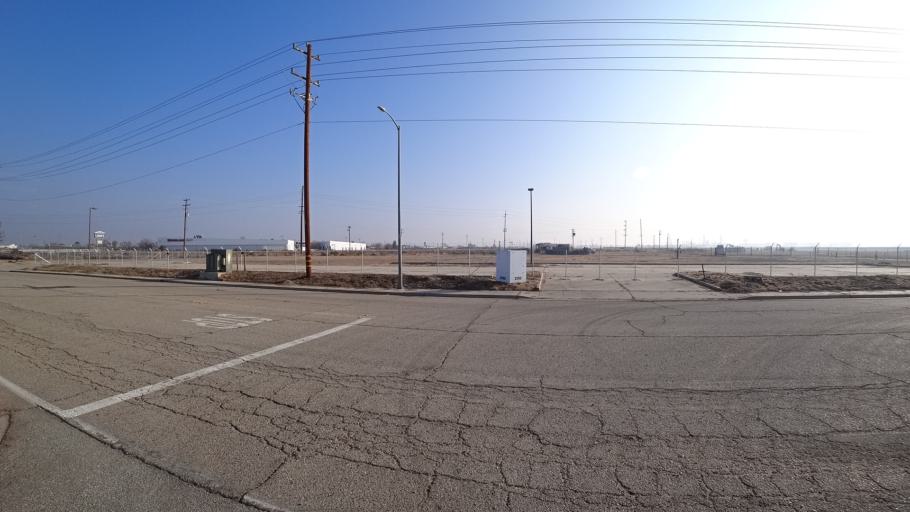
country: US
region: California
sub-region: Kern County
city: Greenacres
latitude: 35.3789
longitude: -119.0922
